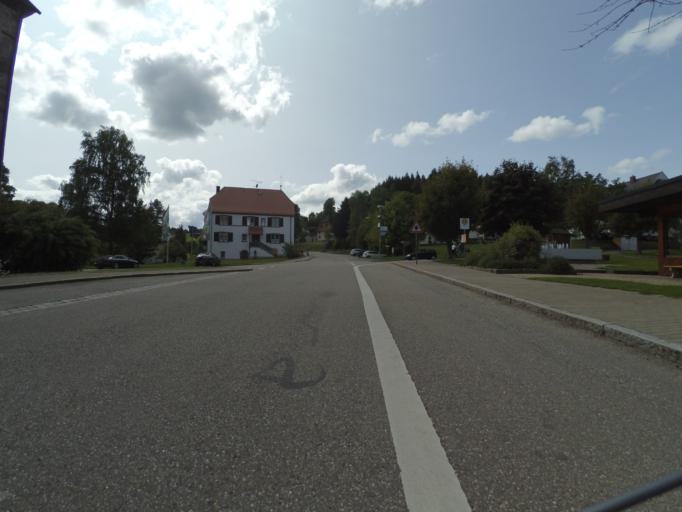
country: DE
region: Baden-Wuerttemberg
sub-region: Freiburg Region
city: Friedenweiler
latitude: 47.9171
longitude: 8.2568
